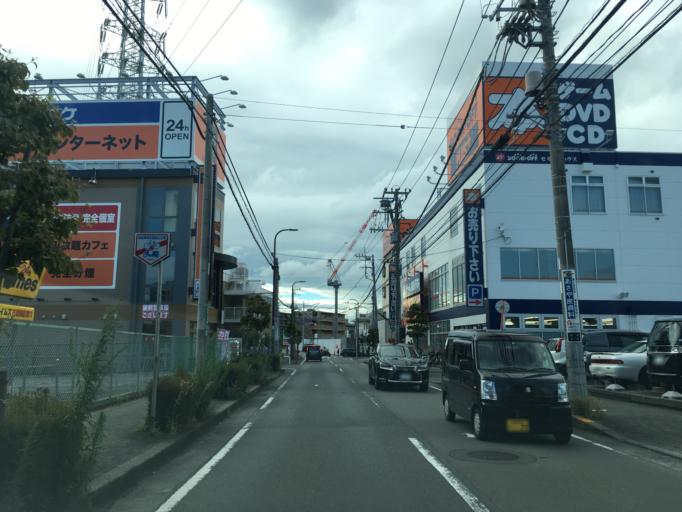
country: JP
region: Tokyo
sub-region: Machida-shi
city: Machida
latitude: 35.5560
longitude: 139.4184
